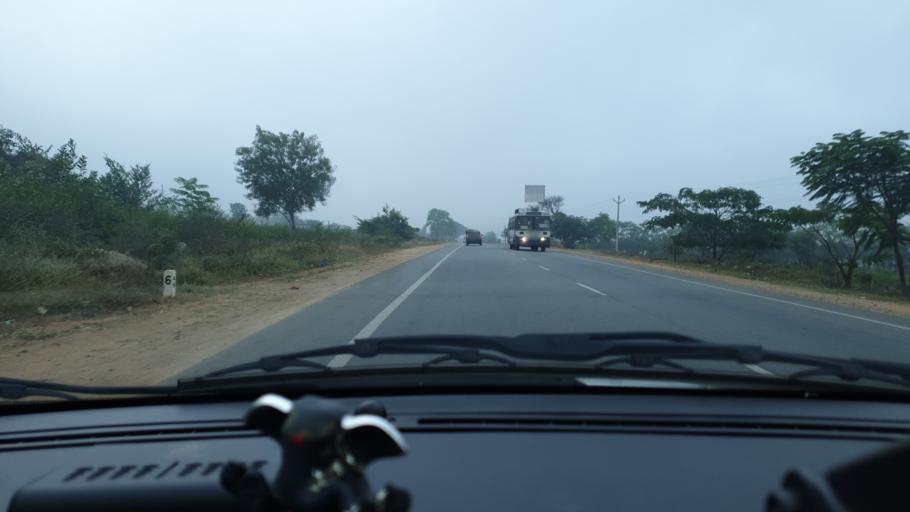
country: IN
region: Telangana
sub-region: Mahbubnagar
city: Farrukhnagar
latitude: 16.9632
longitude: 78.5110
